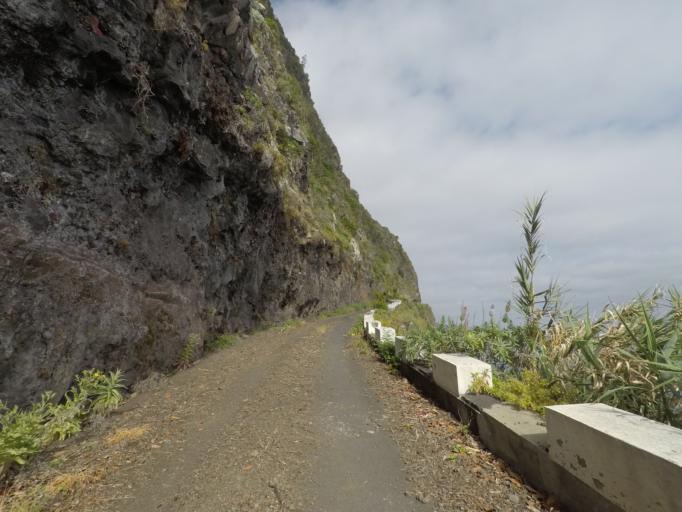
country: PT
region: Madeira
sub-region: Sao Vicente
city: Sao Vicente
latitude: 32.8111
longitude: -17.0622
